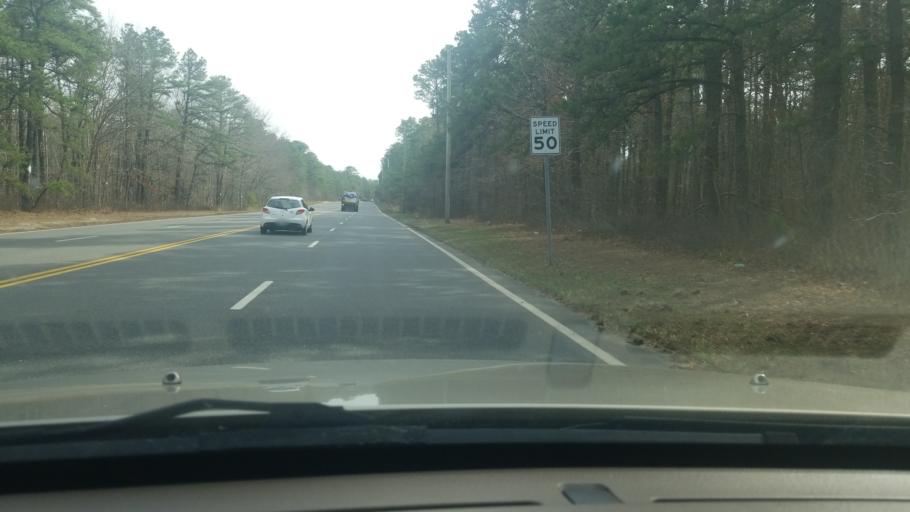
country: US
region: New Jersey
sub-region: Ocean County
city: Vista Center
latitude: 40.1681
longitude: -74.3497
